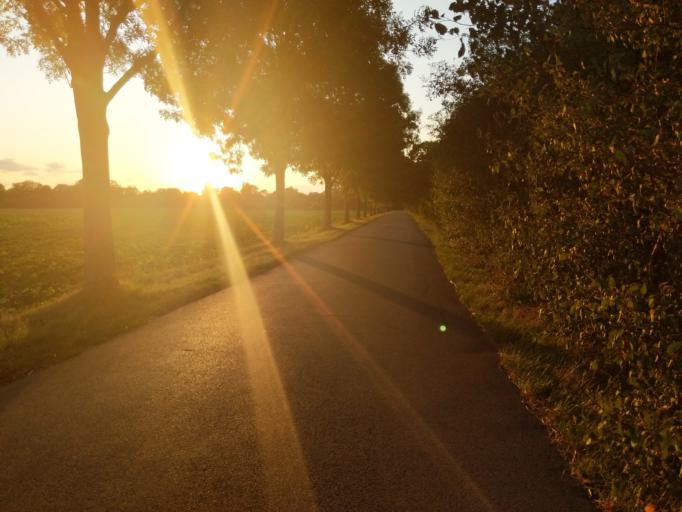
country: DE
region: North Rhine-Westphalia
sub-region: Regierungsbezirk Dusseldorf
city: Krefeld
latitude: 51.3293
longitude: 6.6439
